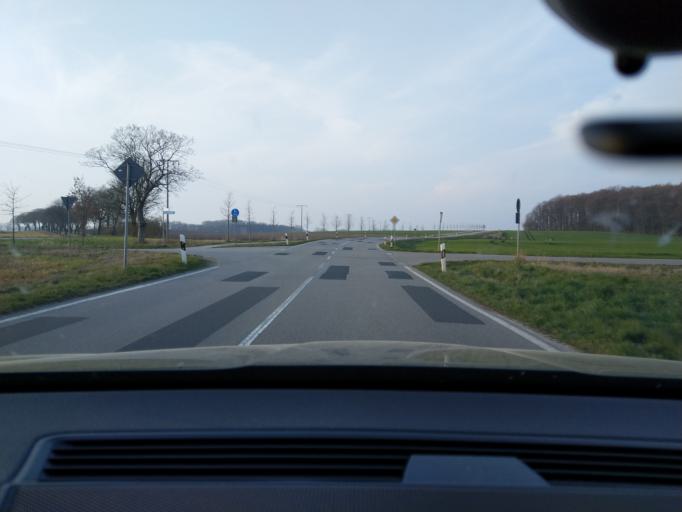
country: DE
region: Mecklenburg-Vorpommern
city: Kramerhof
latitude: 54.3370
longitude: 13.0303
